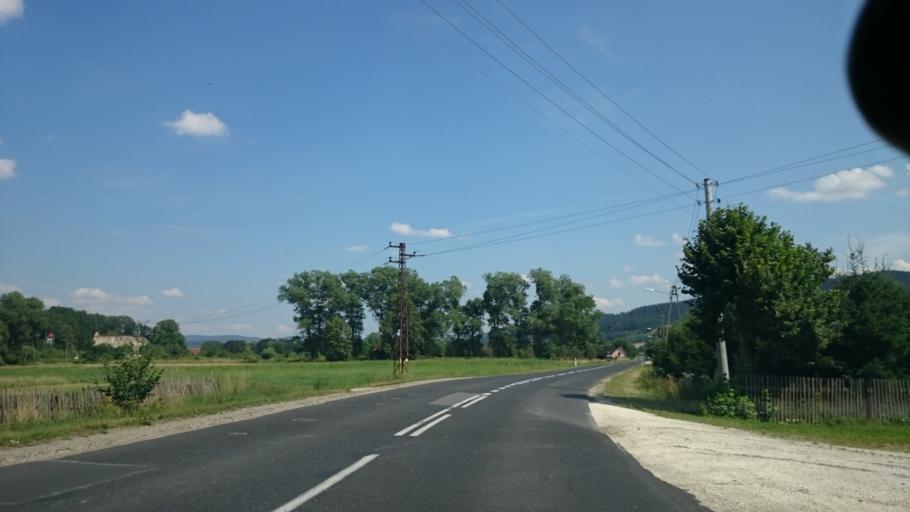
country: PL
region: Lower Silesian Voivodeship
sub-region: Powiat klodzki
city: Ladek-Zdroj
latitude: 50.3513
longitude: 16.7589
